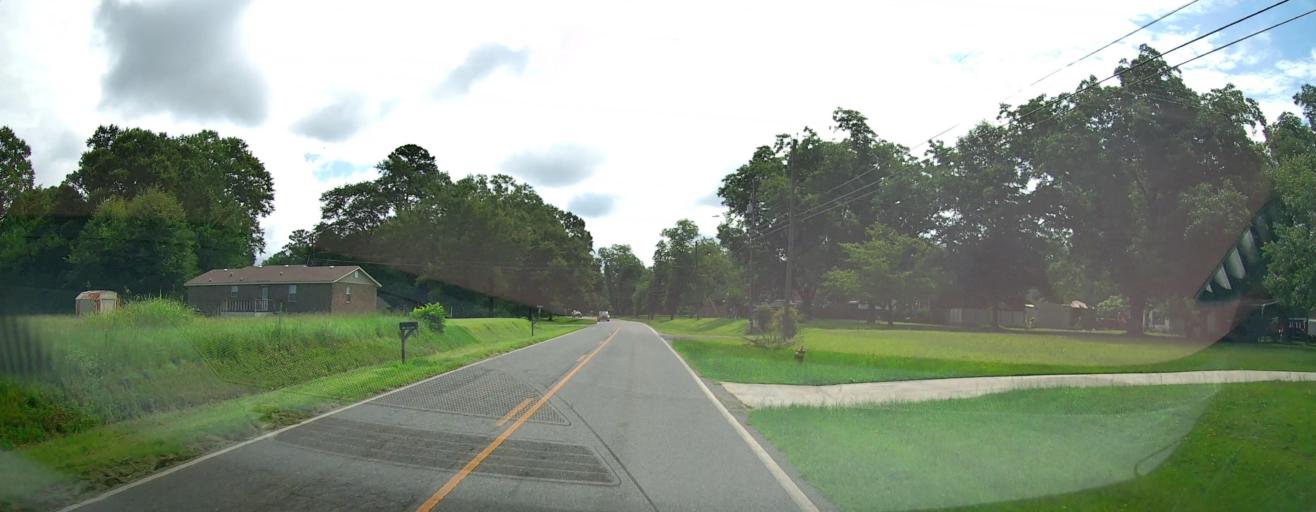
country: US
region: Georgia
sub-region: Peach County
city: Byron
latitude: 32.6464
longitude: -83.7737
